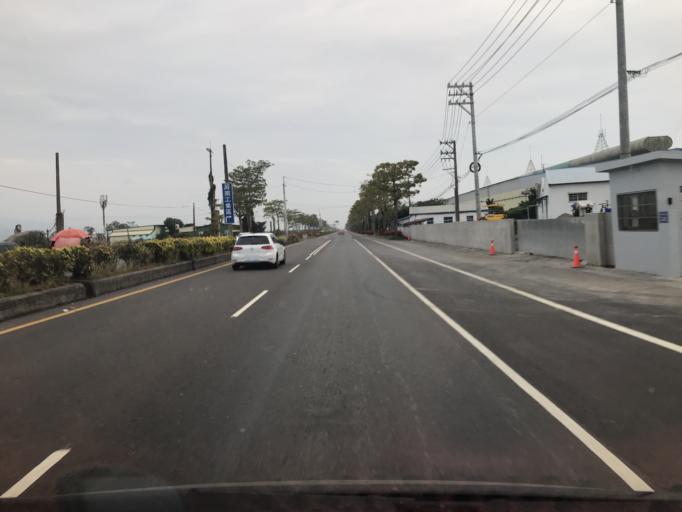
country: TW
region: Taiwan
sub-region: Pingtung
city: Pingtung
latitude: 22.4187
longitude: 120.5837
